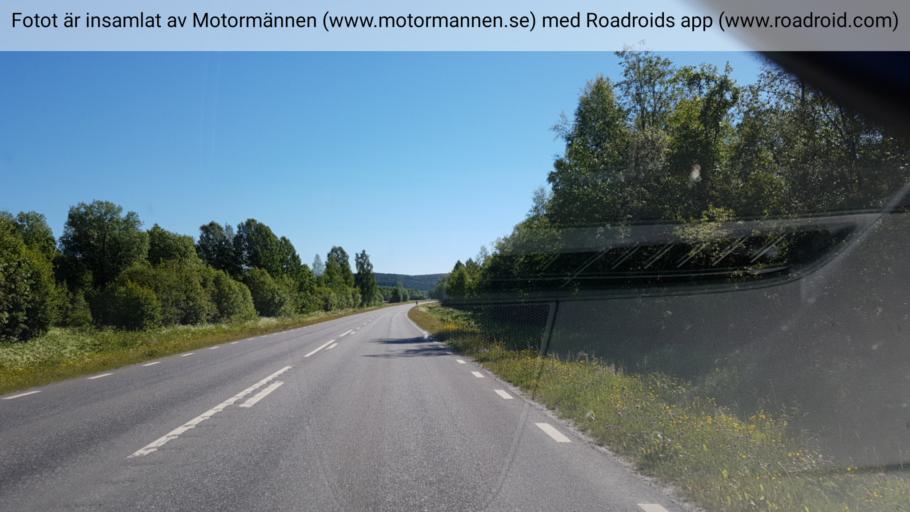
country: SE
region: Norrbotten
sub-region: Bodens Kommun
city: Boden
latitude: 65.8504
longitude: 21.5499
